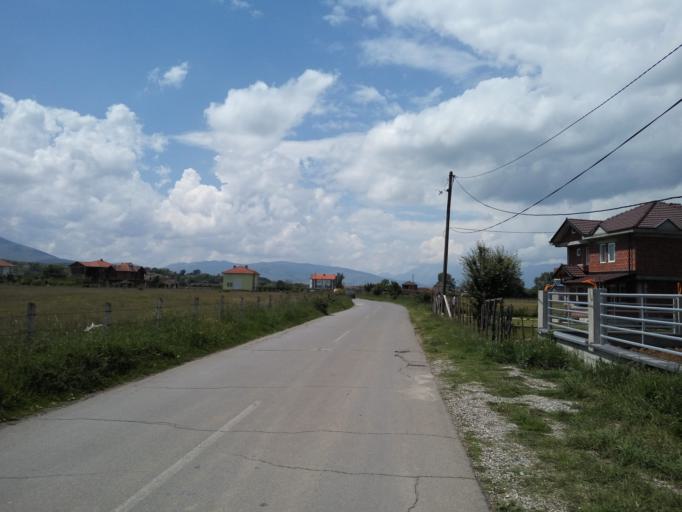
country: XK
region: Gjakova
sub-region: Komuna e Gjakoves
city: Gjakove
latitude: 42.3647
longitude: 20.4231
